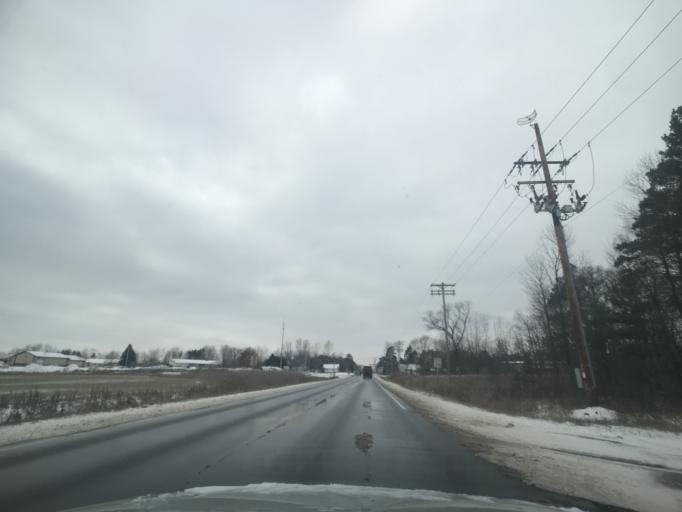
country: US
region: Wisconsin
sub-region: Brown County
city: Suamico
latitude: 44.7209
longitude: -88.0631
